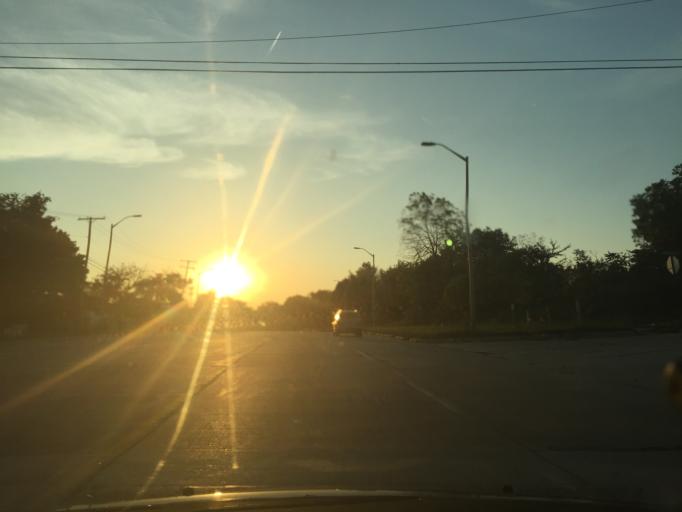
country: US
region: Michigan
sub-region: Oakland County
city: Pontiac
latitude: 42.6489
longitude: -83.2631
